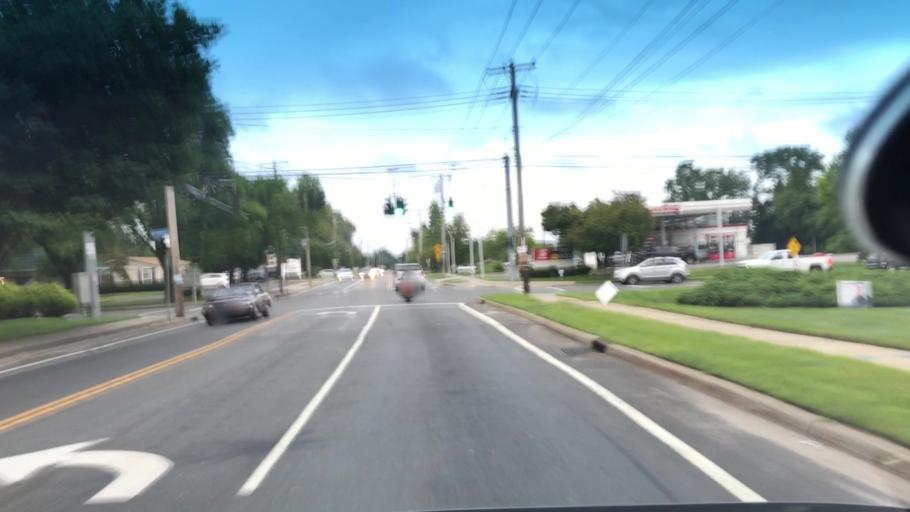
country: US
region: New York
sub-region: Suffolk County
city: Wading River
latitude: 40.9439
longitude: -72.8427
